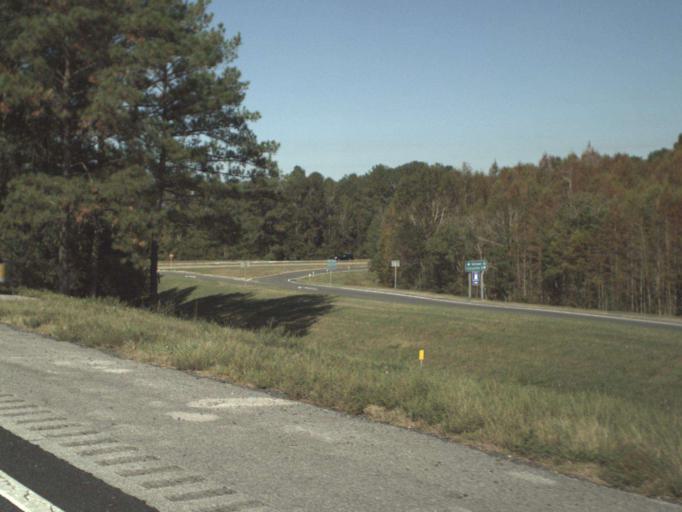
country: US
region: Florida
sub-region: Holmes County
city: Bonifay
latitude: 30.7586
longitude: -85.8107
